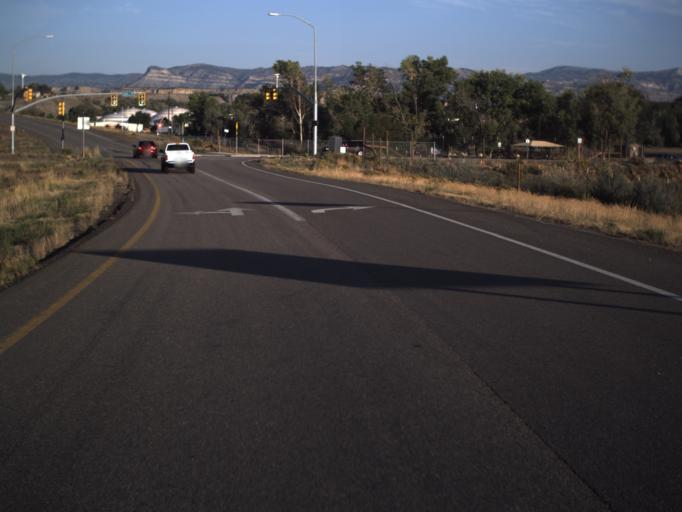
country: US
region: Utah
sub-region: Carbon County
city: Price
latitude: 39.5878
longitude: -110.8106
